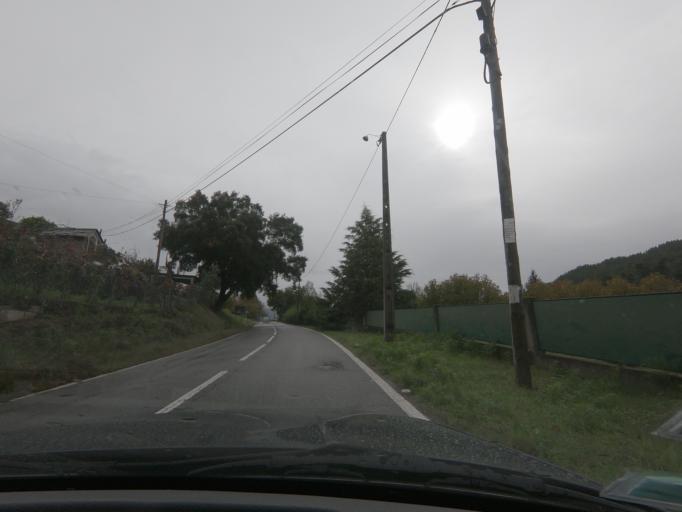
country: PT
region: Vila Real
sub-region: Mondim de Basto
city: Mondim de Basto
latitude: 41.3719
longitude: -7.9352
